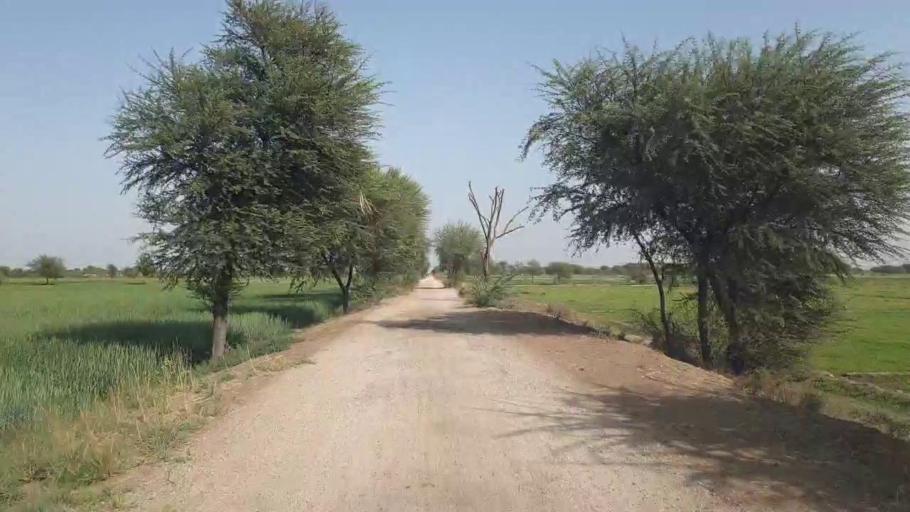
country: PK
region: Sindh
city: Dhoro Naro
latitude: 25.4420
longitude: 69.5286
